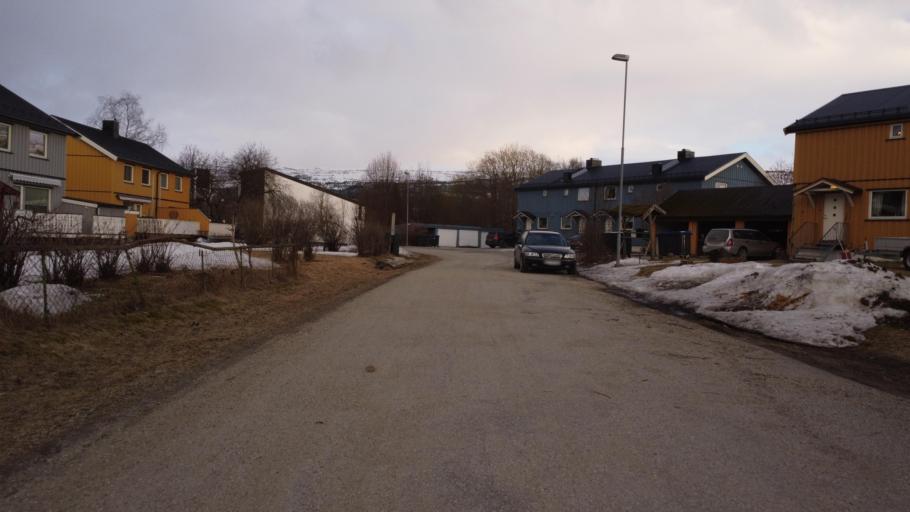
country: NO
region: Nordland
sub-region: Rana
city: Mo i Rana
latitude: 66.3258
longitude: 14.1691
